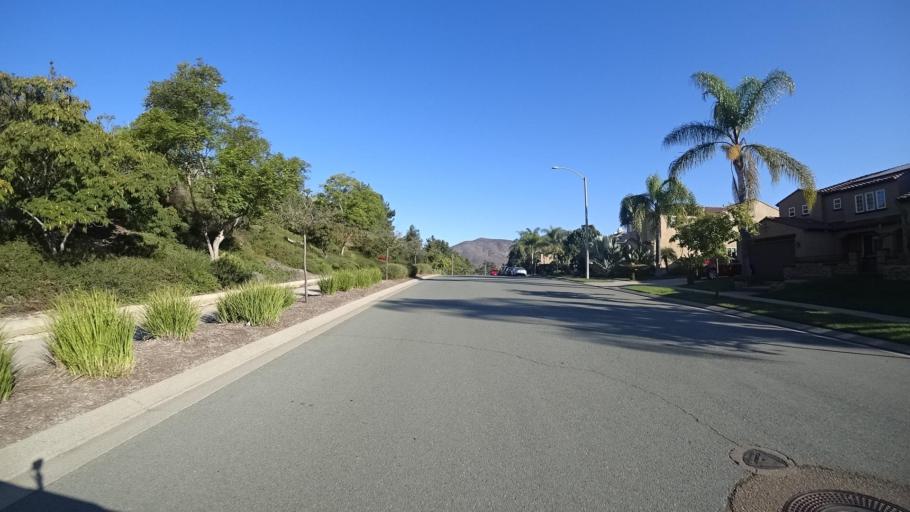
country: US
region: California
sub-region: San Diego County
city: La Presa
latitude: 32.6564
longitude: -116.9452
